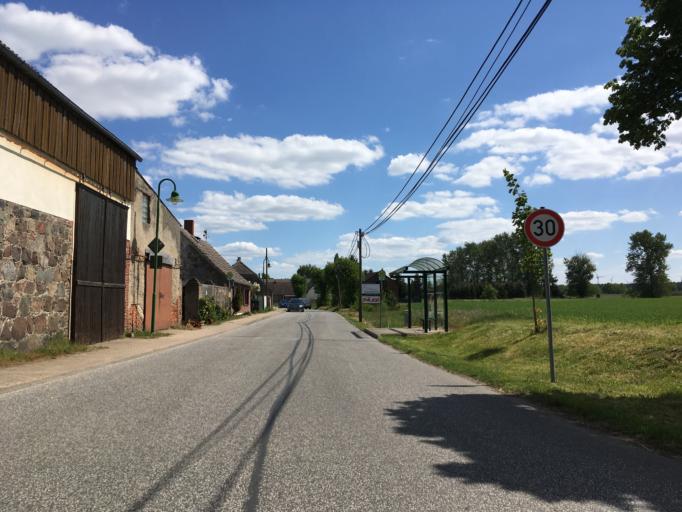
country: DE
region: Brandenburg
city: Biesenthal
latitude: 52.7367
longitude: 13.6600
